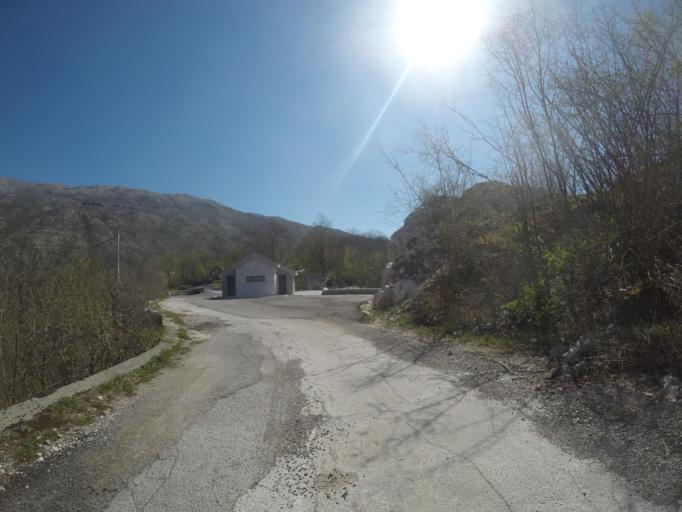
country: ME
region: Danilovgrad
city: Danilovgrad
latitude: 42.5414
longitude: 19.0067
